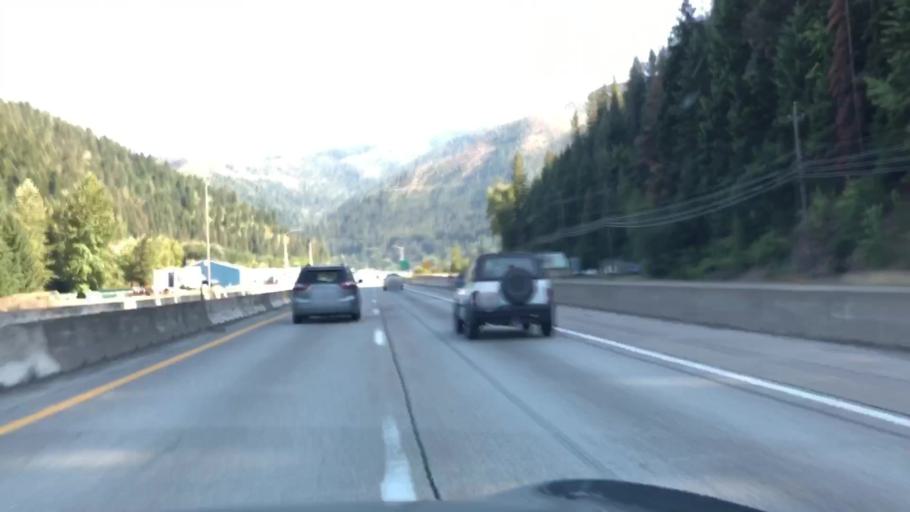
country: US
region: Idaho
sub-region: Shoshone County
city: Wallace
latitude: 47.4827
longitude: -115.9394
